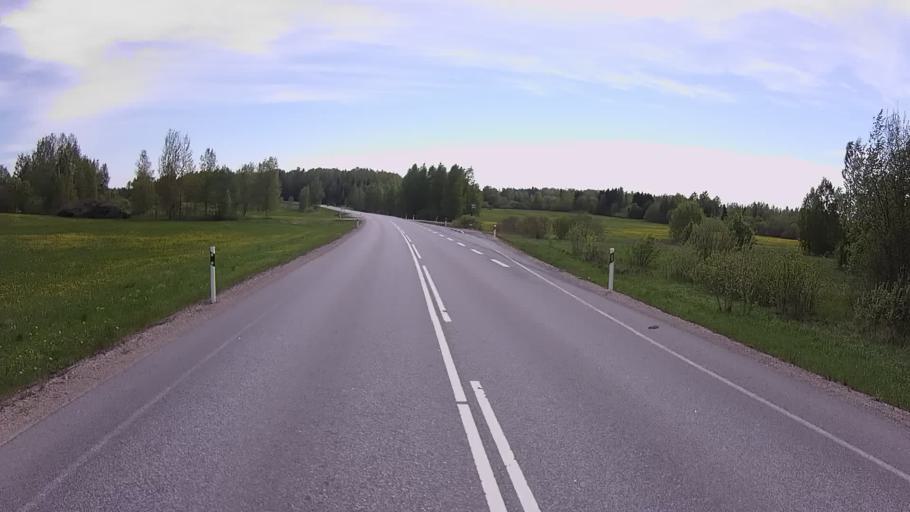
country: EE
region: Valgamaa
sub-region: Valga linn
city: Valga
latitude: 57.7383
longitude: 26.1445
